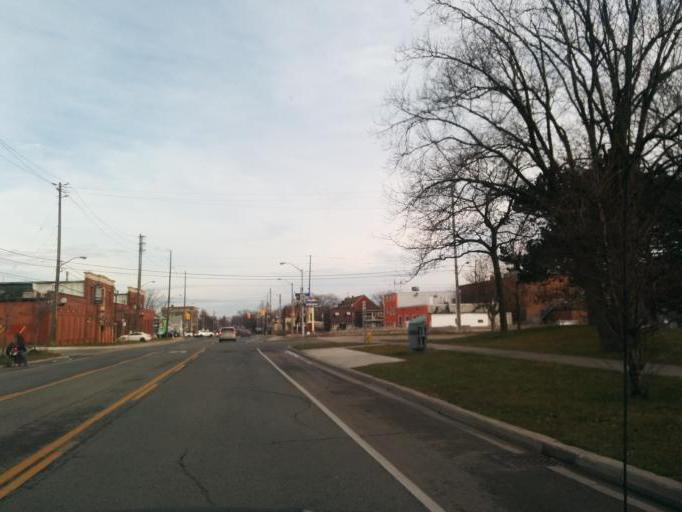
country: CA
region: Ontario
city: Etobicoke
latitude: 43.6028
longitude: -79.5082
